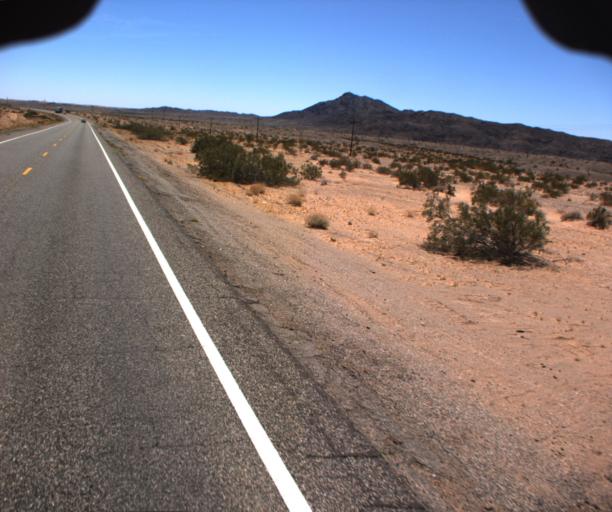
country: US
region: Arizona
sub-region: La Paz County
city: Parker
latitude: 34.0374
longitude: -114.2585
